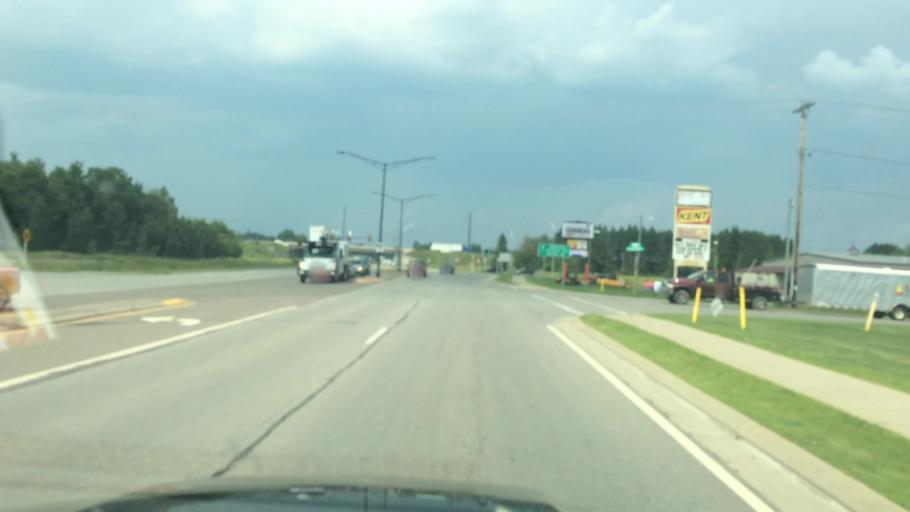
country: US
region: Wisconsin
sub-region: Clark County
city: Abbotsford
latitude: 44.9288
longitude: -90.3153
